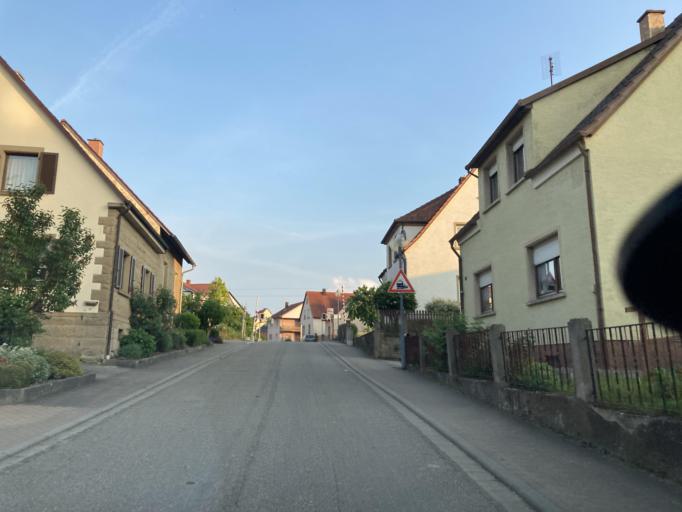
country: DE
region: Baden-Wuerttemberg
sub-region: Karlsruhe Region
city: Sulzfeld
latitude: 49.1077
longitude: 8.8583
